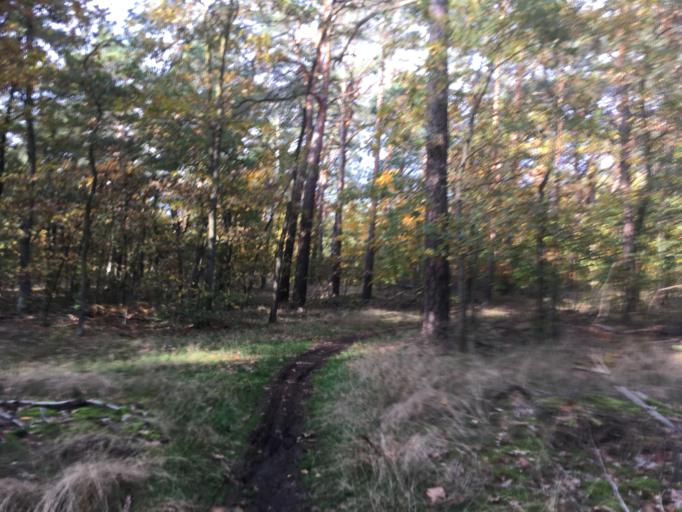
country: DE
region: Berlin
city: Kopenick Bezirk
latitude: 52.4682
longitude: 13.5566
